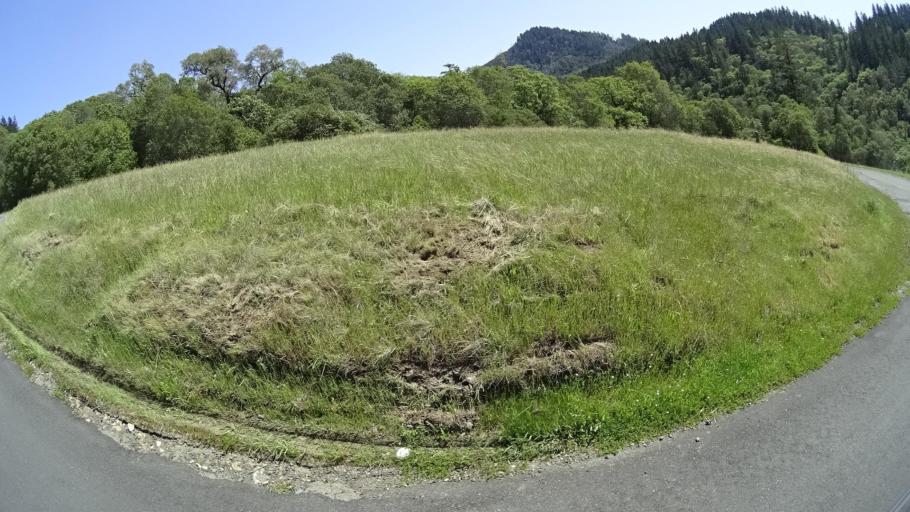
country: US
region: California
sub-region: Humboldt County
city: Redway
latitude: 40.2371
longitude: -123.6327
